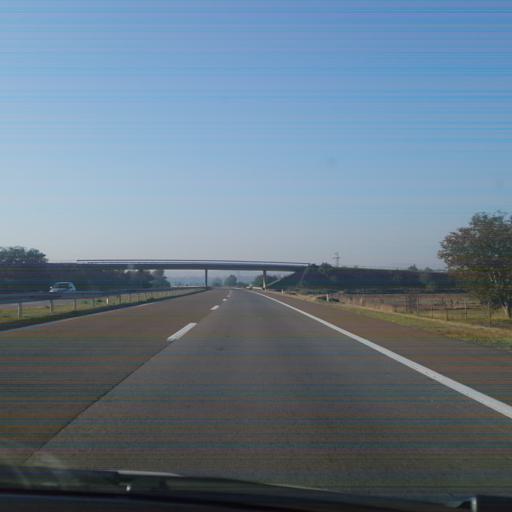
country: RS
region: Central Serbia
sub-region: Nisavski Okrug
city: Merosina
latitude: 43.3164
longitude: 21.8032
